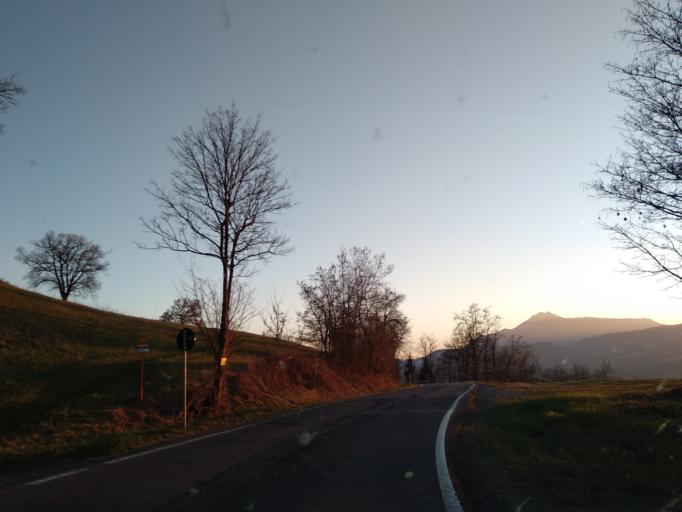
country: IT
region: Emilia-Romagna
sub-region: Provincia di Reggio Emilia
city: Castelnovo ne'Monti
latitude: 44.4221
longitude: 10.4043
